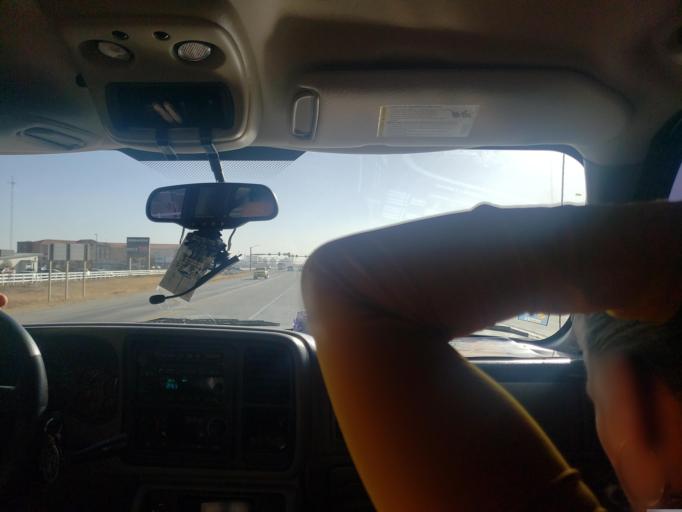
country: US
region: Kansas
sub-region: Finney County
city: Garden City
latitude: 37.9770
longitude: -100.8384
